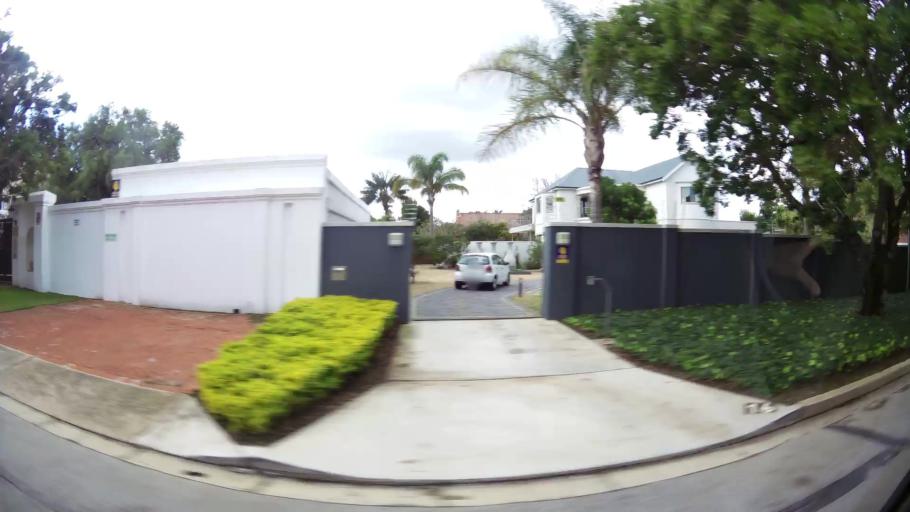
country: ZA
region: Eastern Cape
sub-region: Nelson Mandela Bay Metropolitan Municipality
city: Port Elizabeth
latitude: -33.9605
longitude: 25.5913
